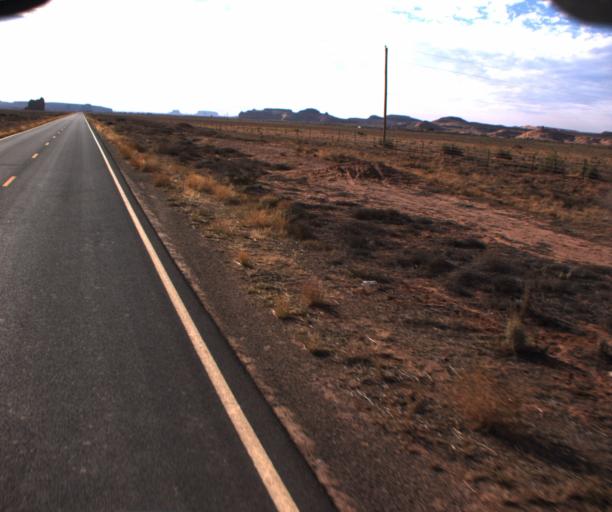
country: US
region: Arizona
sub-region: Apache County
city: Many Farms
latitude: 36.7610
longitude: -109.6502
